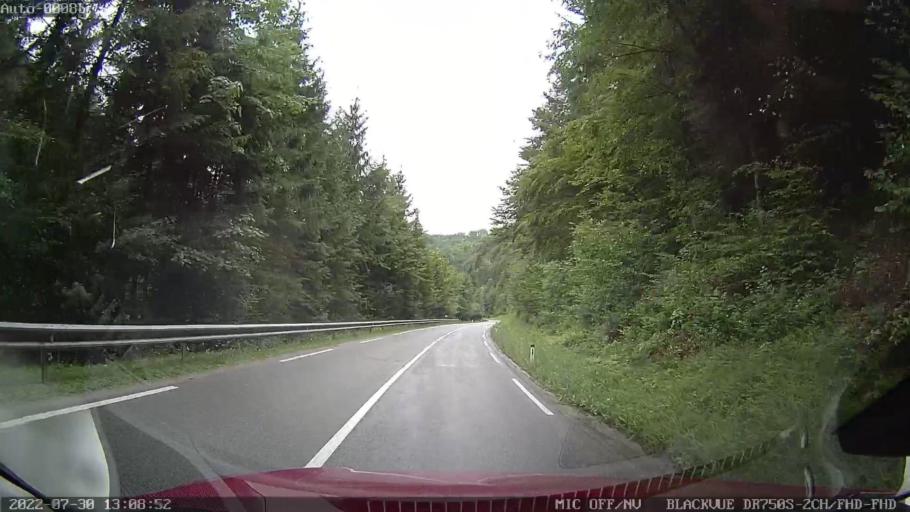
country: SI
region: Dolenjske Toplice
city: Dolenjske Toplice
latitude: 45.6818
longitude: 15.0976
